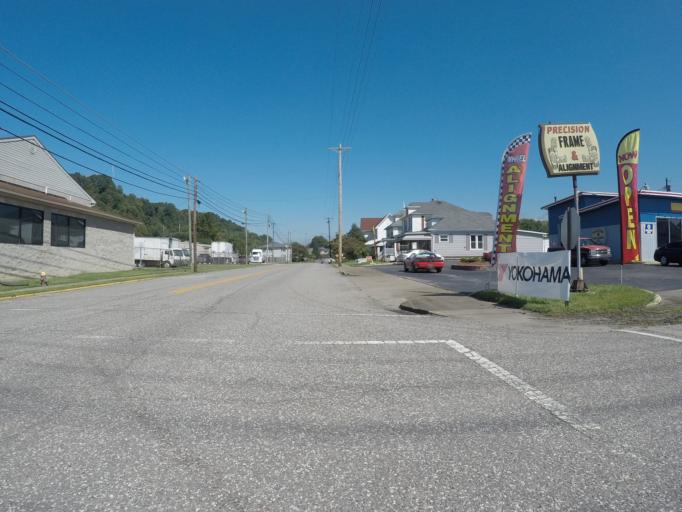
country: US
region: Kentucky
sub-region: Boyd County
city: Catlettsburg
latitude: 38.4059
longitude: -82.5989
